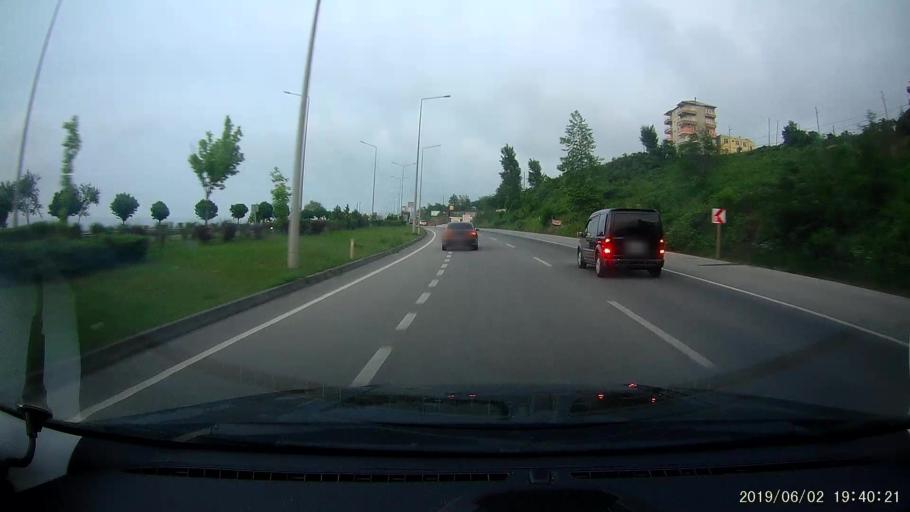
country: TR
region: Giresun
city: Kesap
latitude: 40.9145
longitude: 38.4580
